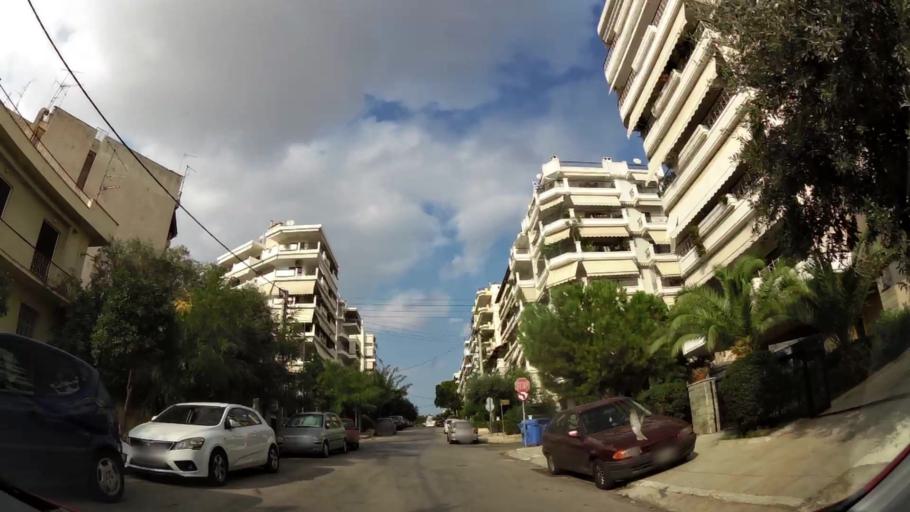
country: GR
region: Attica
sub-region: Nomarchia Athinas
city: Nea Smyrni
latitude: 37.9408
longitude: 23.7212
